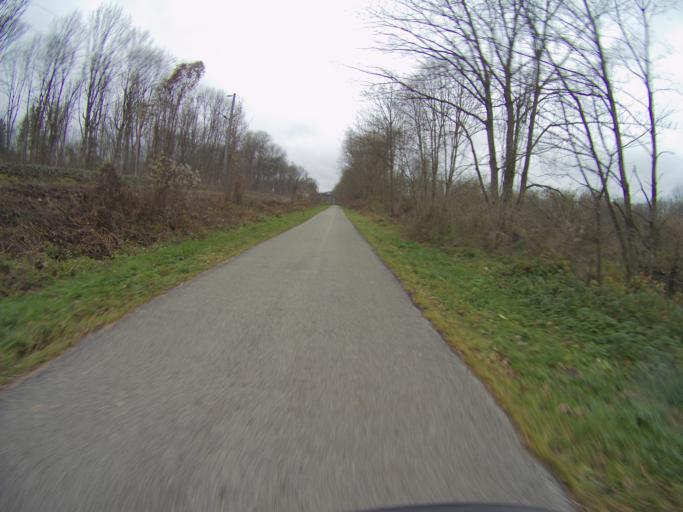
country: DE
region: Bavaria
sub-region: Upper Bavaria
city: Marzling
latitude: 48.4081
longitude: 11.7829
